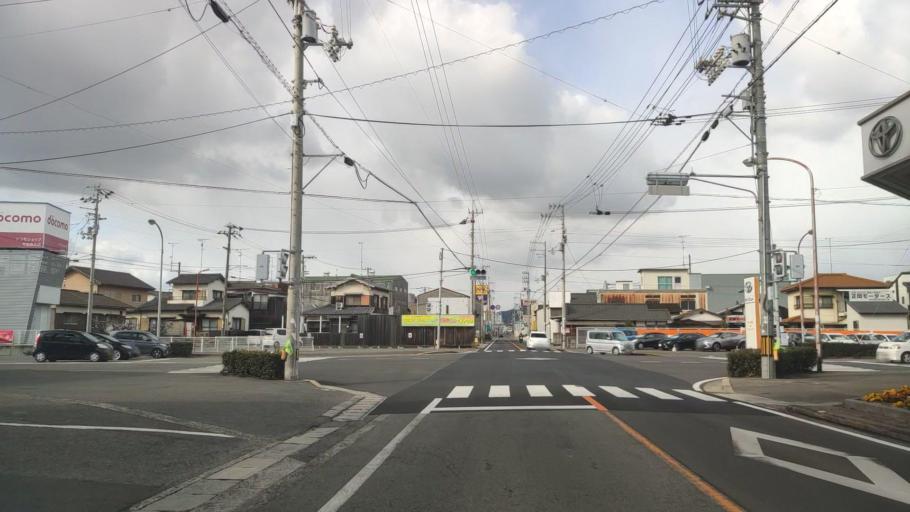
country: JP
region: Ehime
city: Saijo
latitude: 34.0515
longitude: 133.0125
